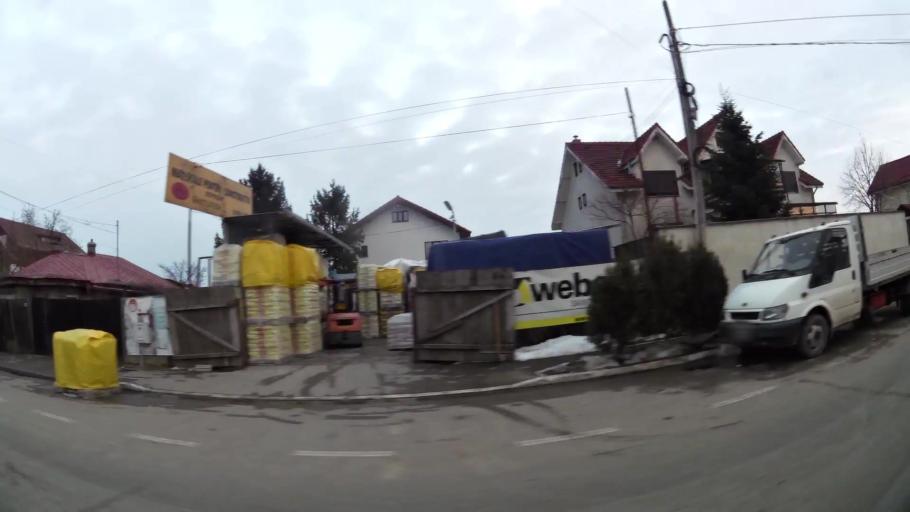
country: RO
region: Ilfov
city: Dobroesti
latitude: 44.4554
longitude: 26.1854
